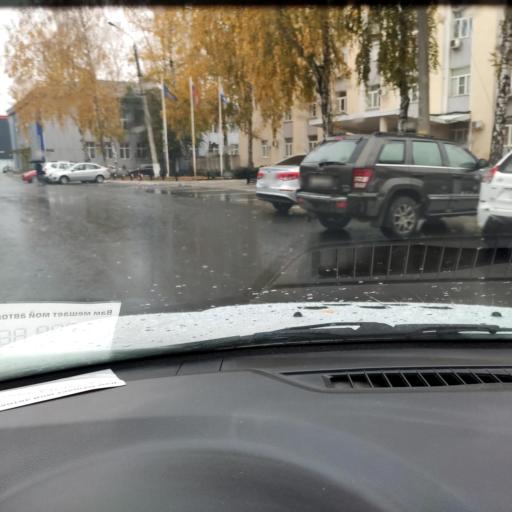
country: RU
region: Samara
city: Tol'yatti
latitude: 53.5187
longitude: 49.4580
